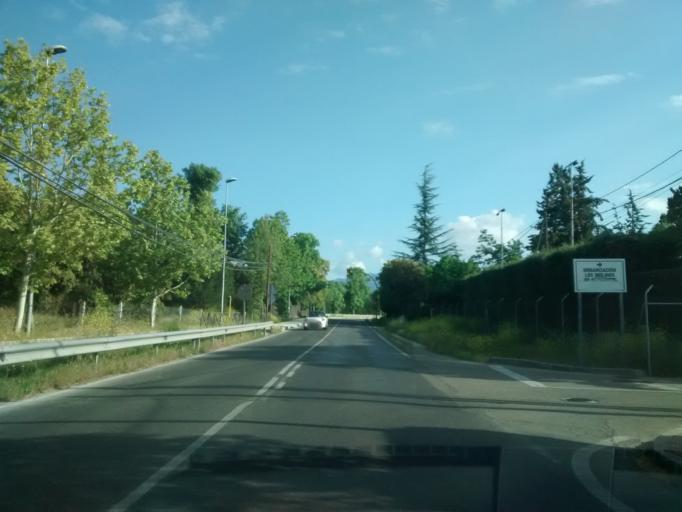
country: ES
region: Madrid
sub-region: Provincia de Madrid
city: Alpedrete
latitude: 40.6464
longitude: -4.0220
